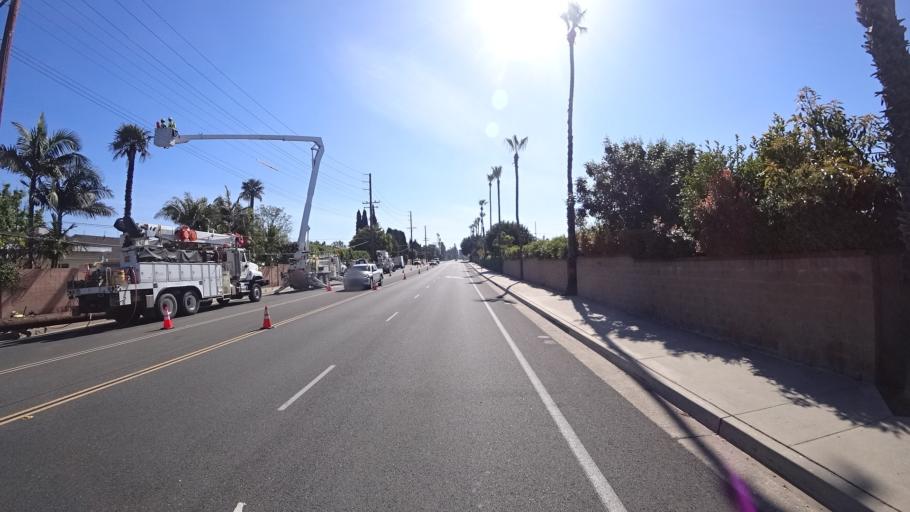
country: US
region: California
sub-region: Orange County
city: Villa Park
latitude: 33.8176
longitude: -117.8220
